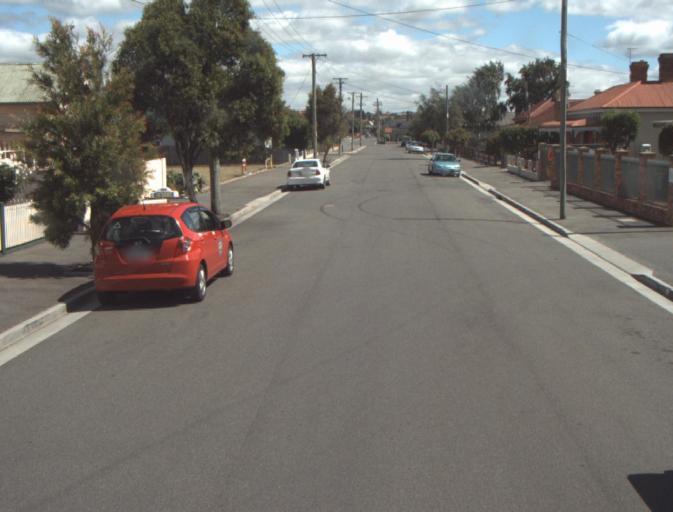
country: AU
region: Tasmania
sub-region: Launceston
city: Launceston
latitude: -41.4214
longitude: 147.1394
